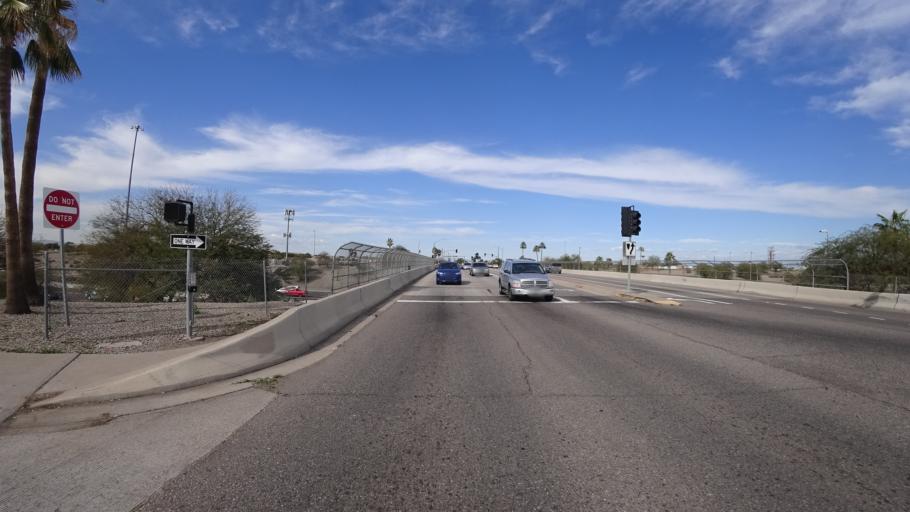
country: US
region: Arizona
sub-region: Maricopa County
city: Tolleson
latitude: 33.4618
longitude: -112.2554
